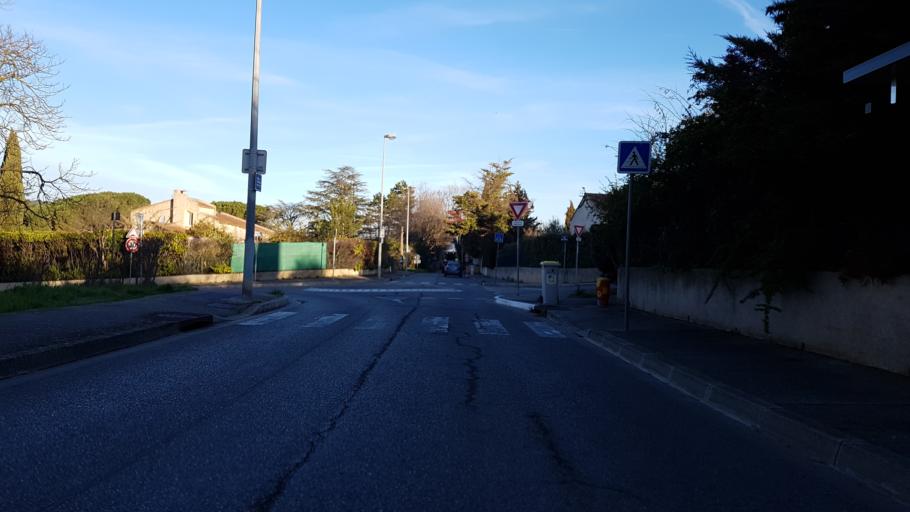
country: FR
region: Provence-Alpes-Cote d'Azur
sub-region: Departement des Bouches-du-Rhone
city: Bouc-Bel-Air
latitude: 43.4894
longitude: 5.4162
